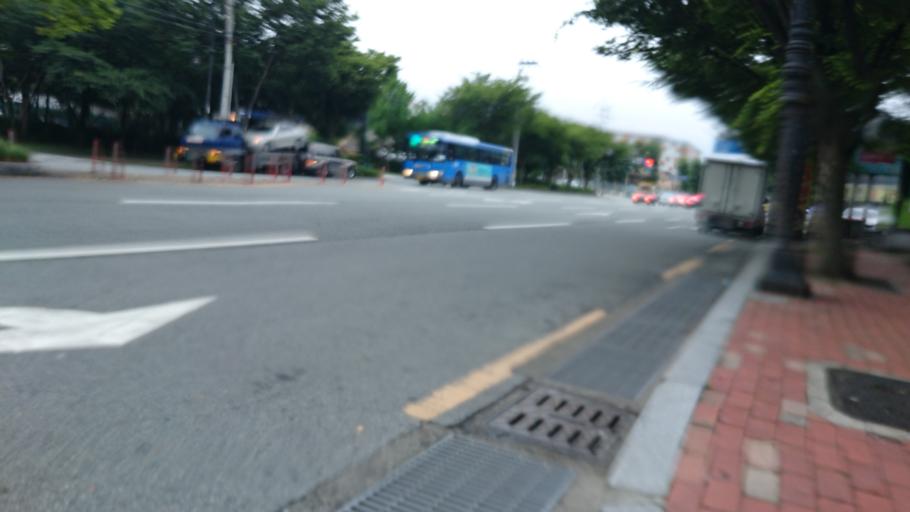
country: KR
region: Daegu
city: Daegu
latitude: 35.8672
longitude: 128.6386
